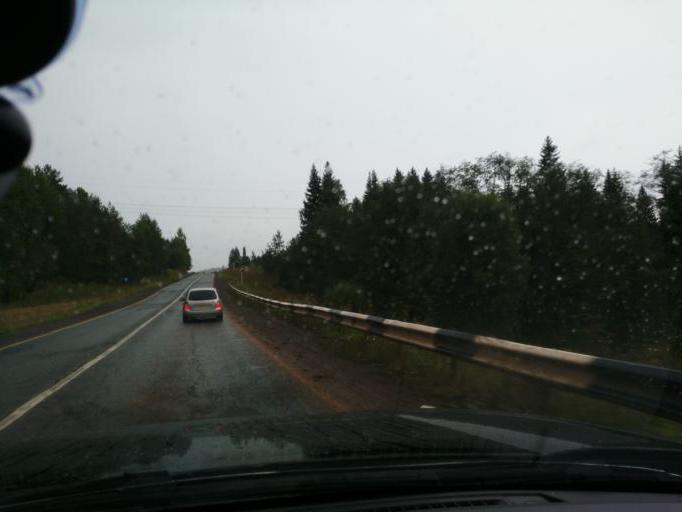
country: RU
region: Perm
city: Barda
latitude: 56.8919
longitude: 55.7516
